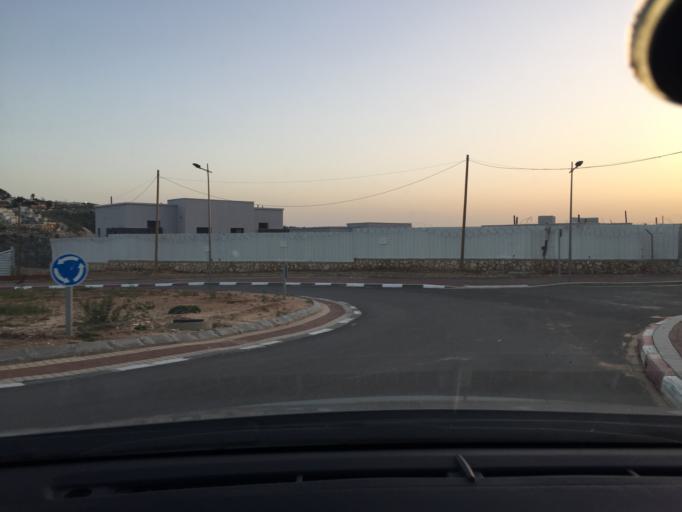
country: PS
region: West Bank
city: Rafat
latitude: 32.0671
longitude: 35.0466
